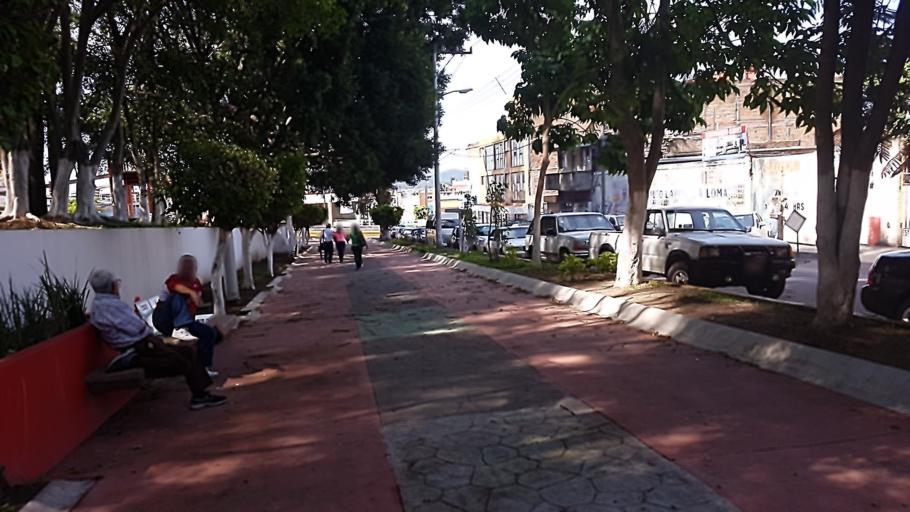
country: MX
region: Nayarit
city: Tepic
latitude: 21.5043
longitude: -104.8971
